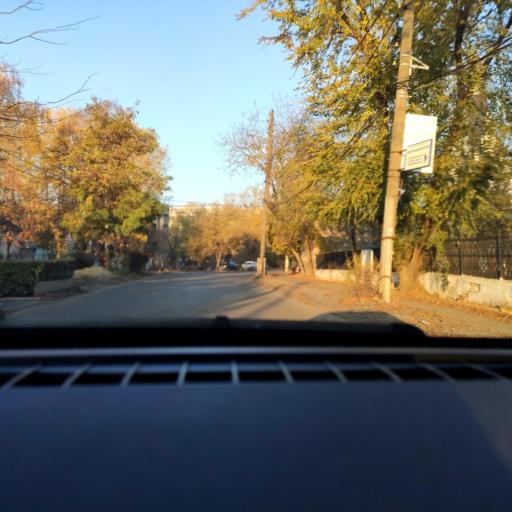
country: RU
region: Voronezj
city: Voronezh
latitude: 51.6754
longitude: 39.2598
